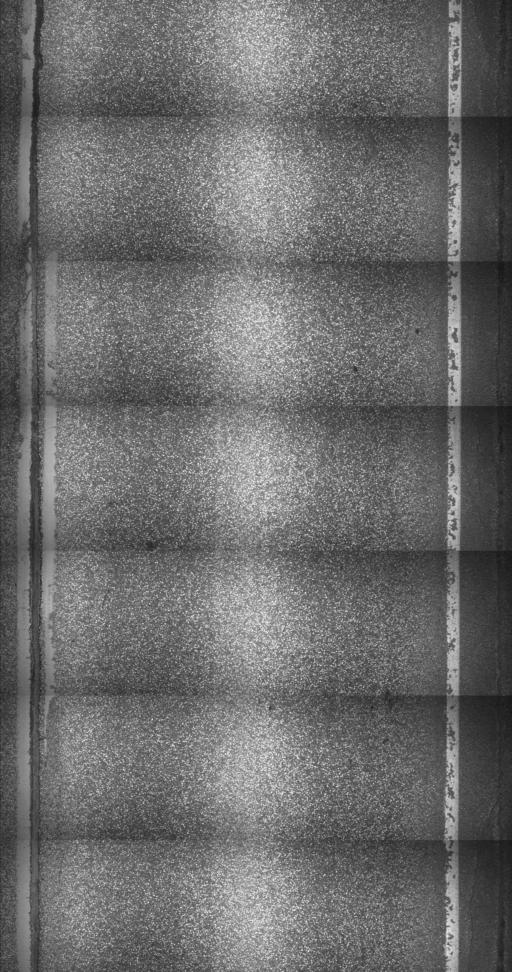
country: US
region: Vermont
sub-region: Washington County
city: Montpelier
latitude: 44.3204
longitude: -72.5779
